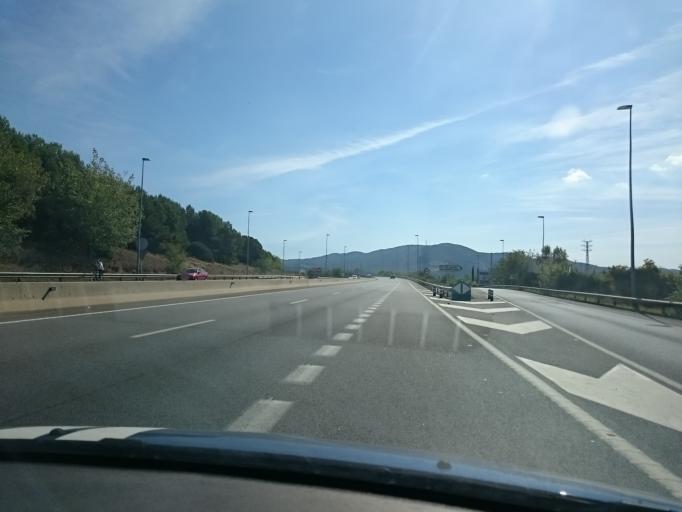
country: ES
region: Catalonia
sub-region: Provincia de Barcelona
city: Santa Perpetua de Mogoda
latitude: 41.5343
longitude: 2.1945
